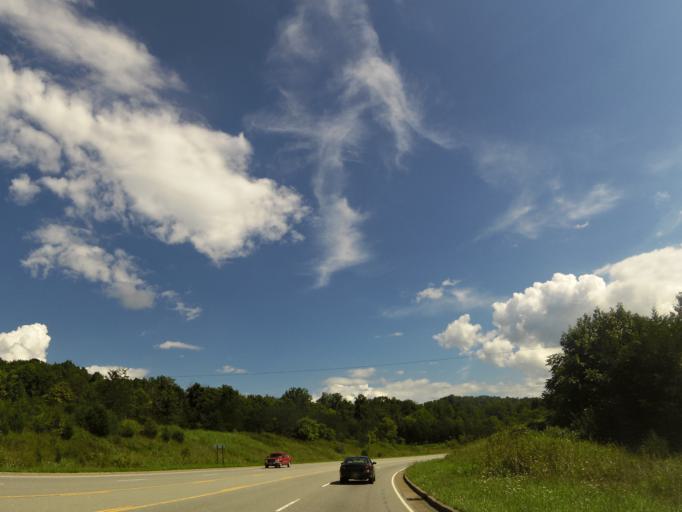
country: US
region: Tennessee
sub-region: Claiborne County
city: Tazewell
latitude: 36.4552
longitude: -83.5654
